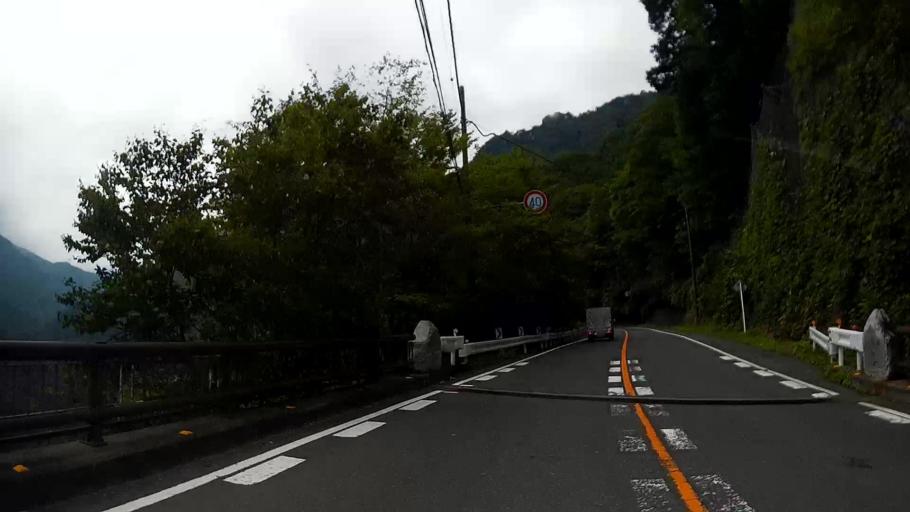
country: JP
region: Yamanashi
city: Enzan
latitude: 35.9208
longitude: 138.8308
